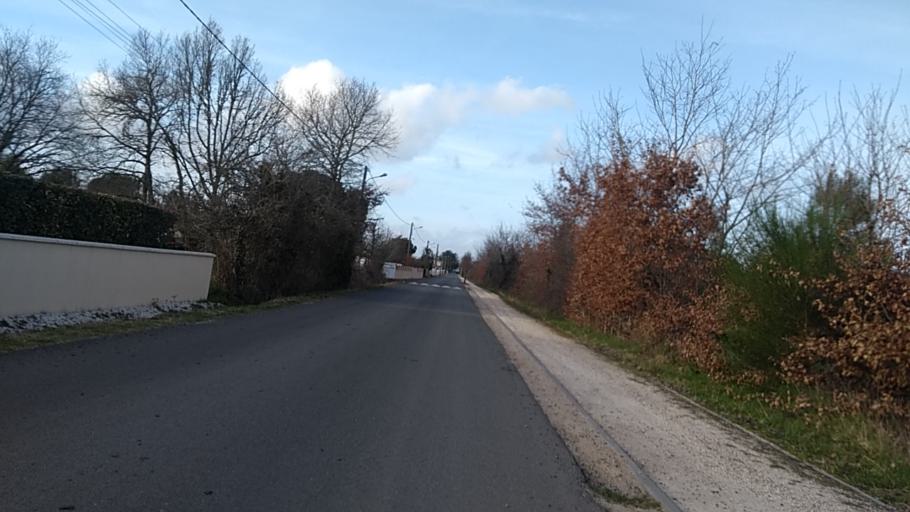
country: FR
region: Aquitaine
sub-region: Departement de la Gironde
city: Le Barp
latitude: 44.5975
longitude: -0.7681
